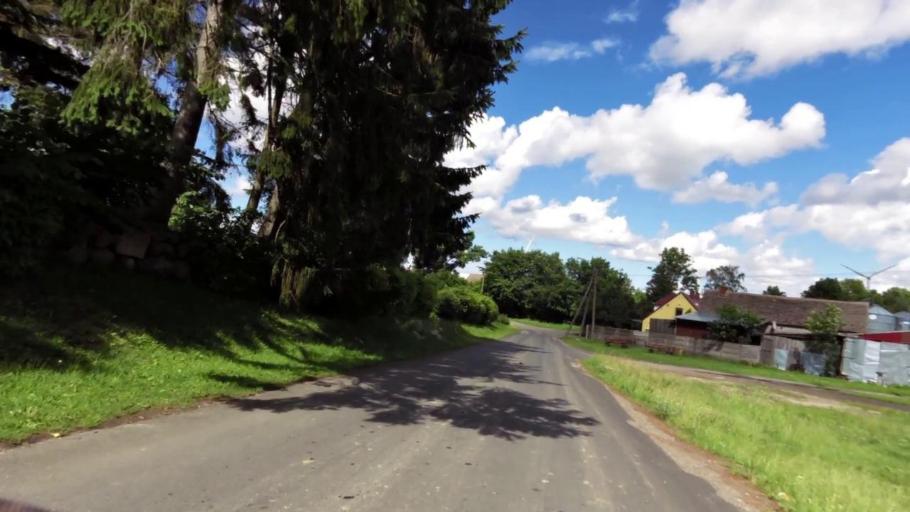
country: PL
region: West Pomeranian Voivodeship
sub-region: Powiat slawienski
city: Slawno
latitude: 54.5108
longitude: 16.7000
